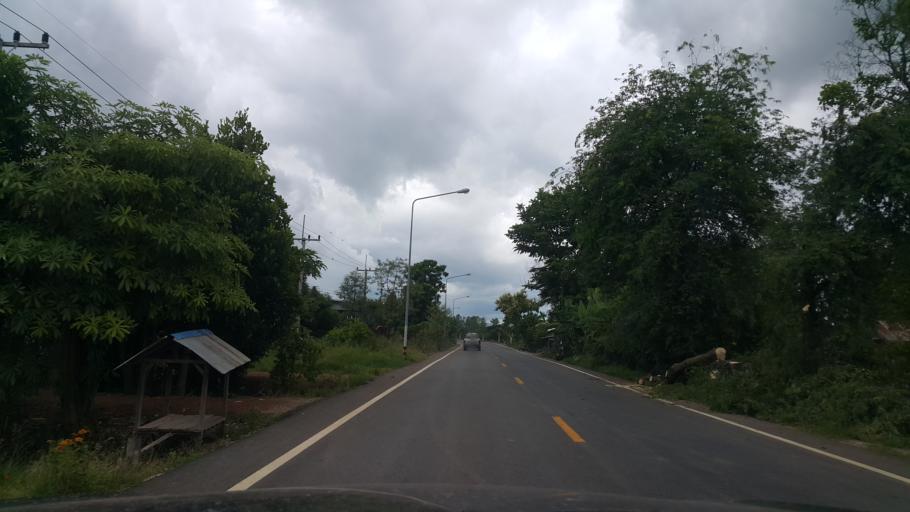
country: TH
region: Sukhothai
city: Sukhothai
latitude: 16.9155
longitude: 99.8648
